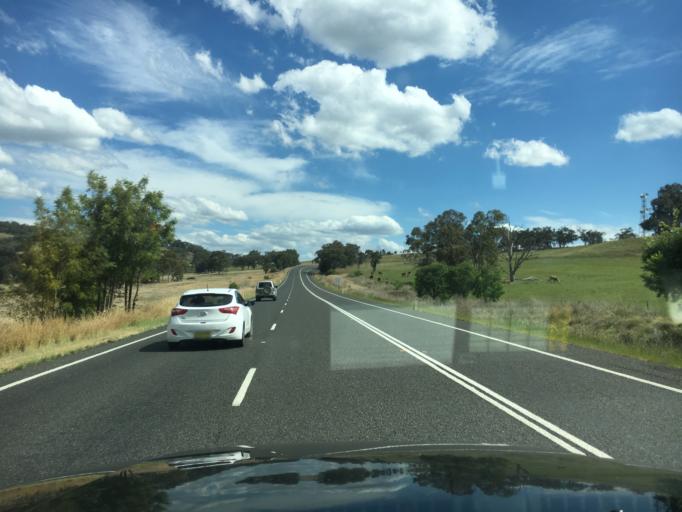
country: AU
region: New South Wales
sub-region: Liverpool Plains
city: Quirindi
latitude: -31.4359
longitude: 150.8819
